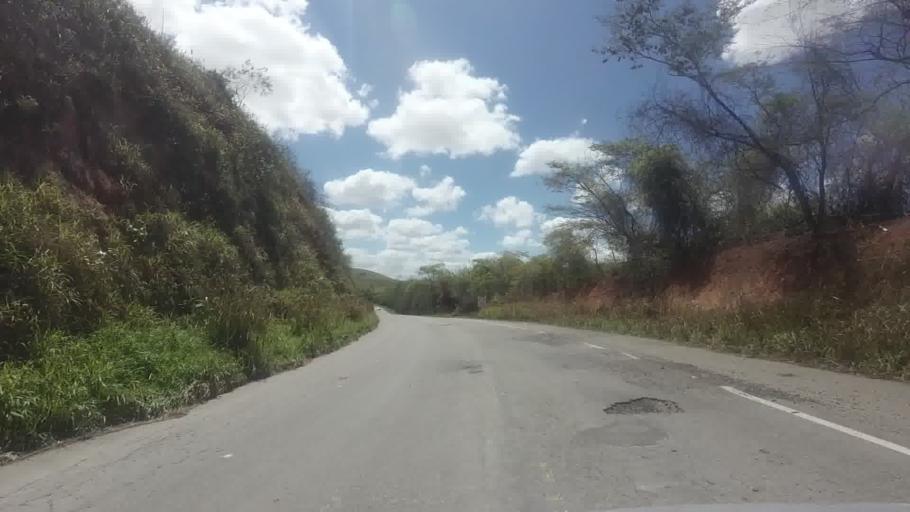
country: BR
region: Rio de Janeiro
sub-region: Santo Antonio De Padua
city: Santo Antonio de Padua
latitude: -21.6579
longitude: -42.3057
